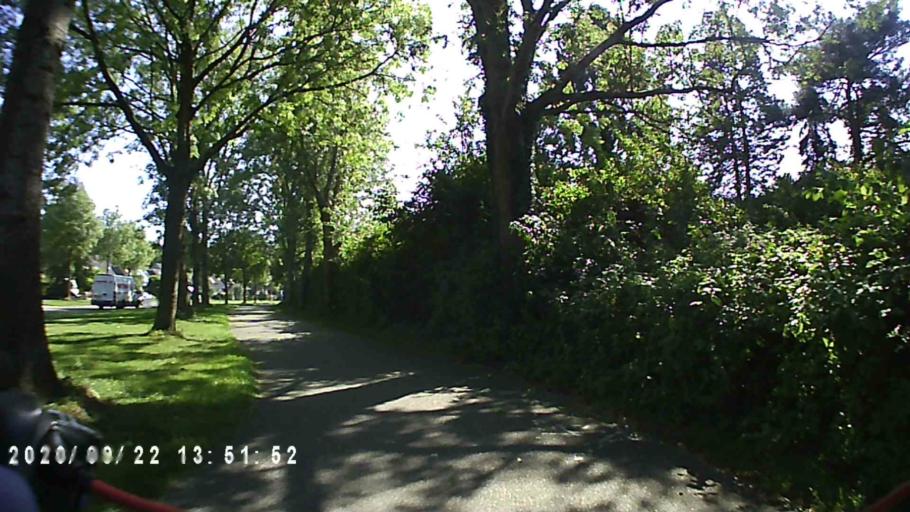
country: NL
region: Groningen
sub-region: Gemeente Leek
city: Leek
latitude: 53.1333
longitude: 6.4127
